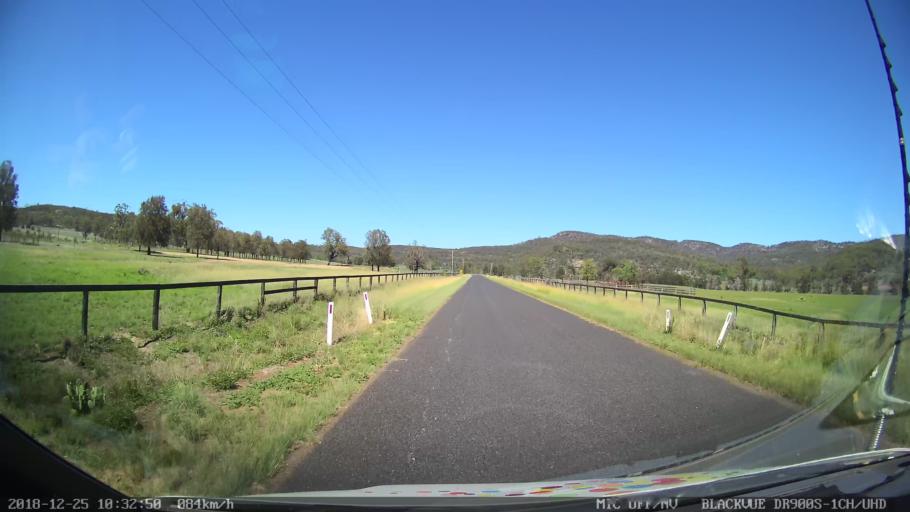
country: AU
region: New South Wales
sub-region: Upper Hunter Shire
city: Merriwa
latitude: -32.3780
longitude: 150.4134
